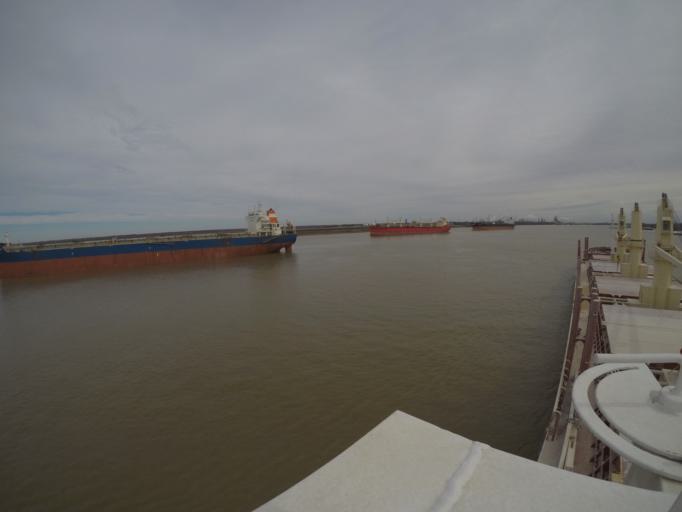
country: US
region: Louisiana
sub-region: Saint Charles Parish
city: Montz
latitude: 29.9947
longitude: -90.4422
